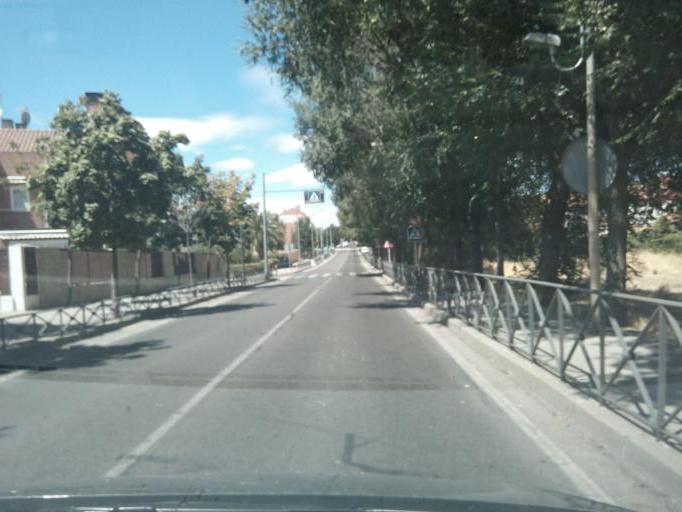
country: ES
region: Madrid
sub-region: Provincia de Madrid
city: Daganzo de Arriba
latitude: 40.5423
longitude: -3.4558
